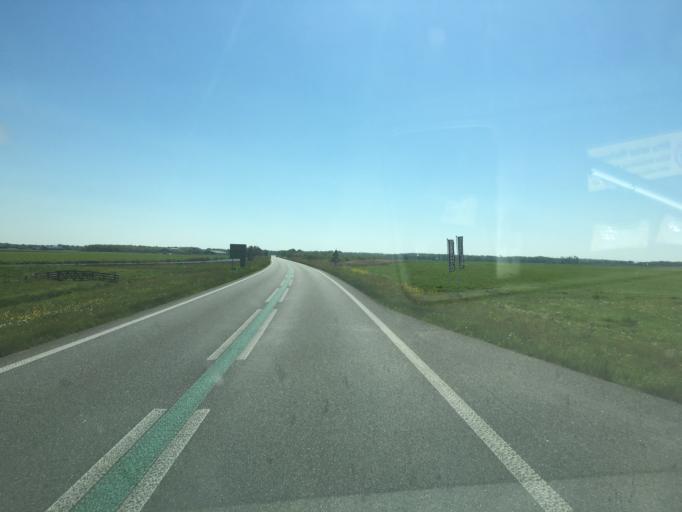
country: NL
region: Friesland
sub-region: Sudwest Fryslan
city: Koudum
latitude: 52.8838
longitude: 5.4913
